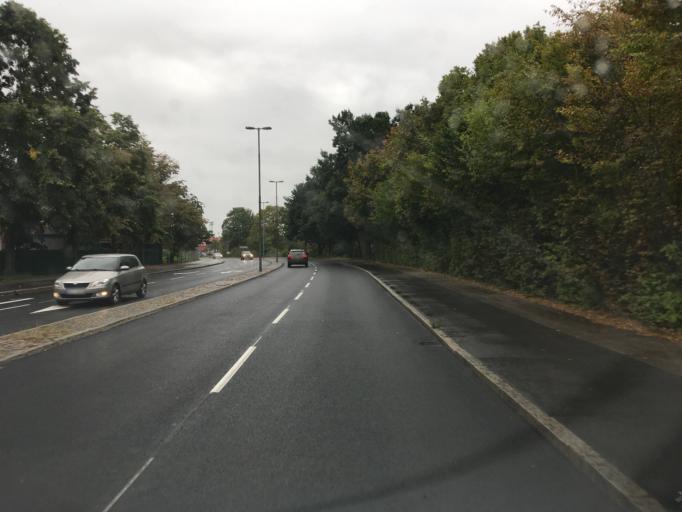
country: SE
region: Skane
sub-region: Lunds Kommun
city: Lund
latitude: 55.7019
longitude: 13.1769
